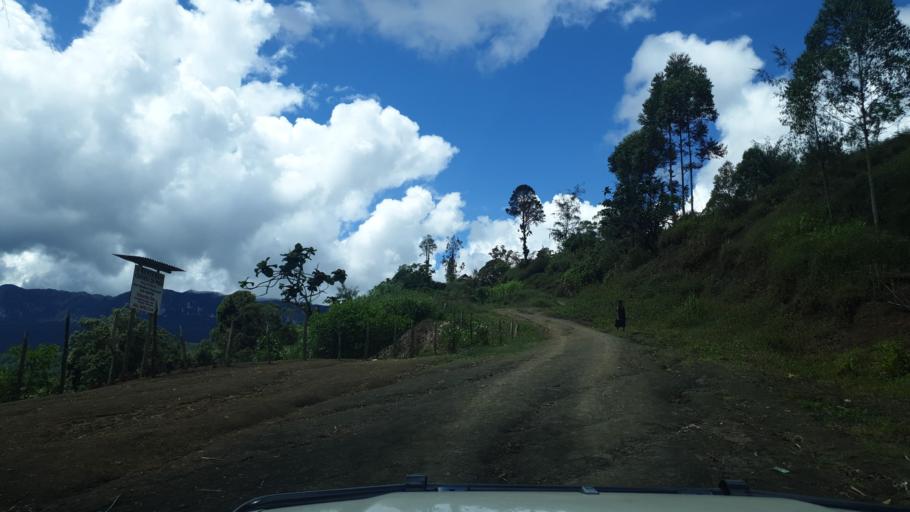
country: PG
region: Eastern Highlands
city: Goroka
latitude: -6.2771
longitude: 145.1862
